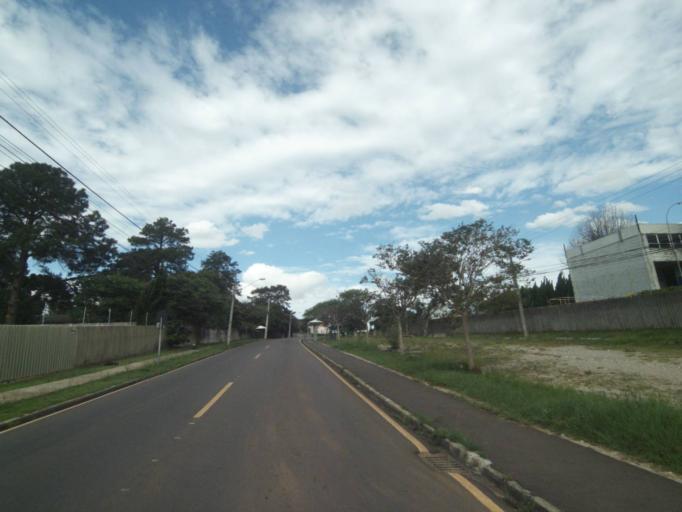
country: BR
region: Parana
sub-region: Curitiba
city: Curitiba
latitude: -25.4971
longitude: -49.3173
